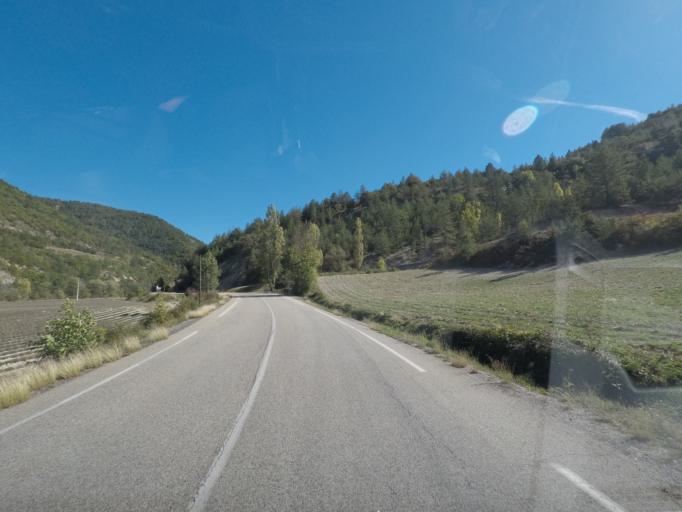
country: FR
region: Rhone-Alpes
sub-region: Departement de la Drome
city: Buis-les-Baronnies
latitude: 44.3873
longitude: 5.3880
